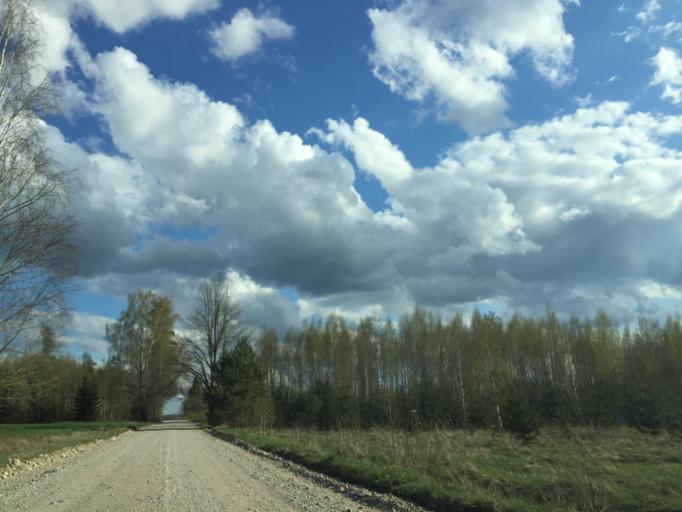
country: LV
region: Beverina
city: Murmuiza
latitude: 57.3848
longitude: 25.4850
